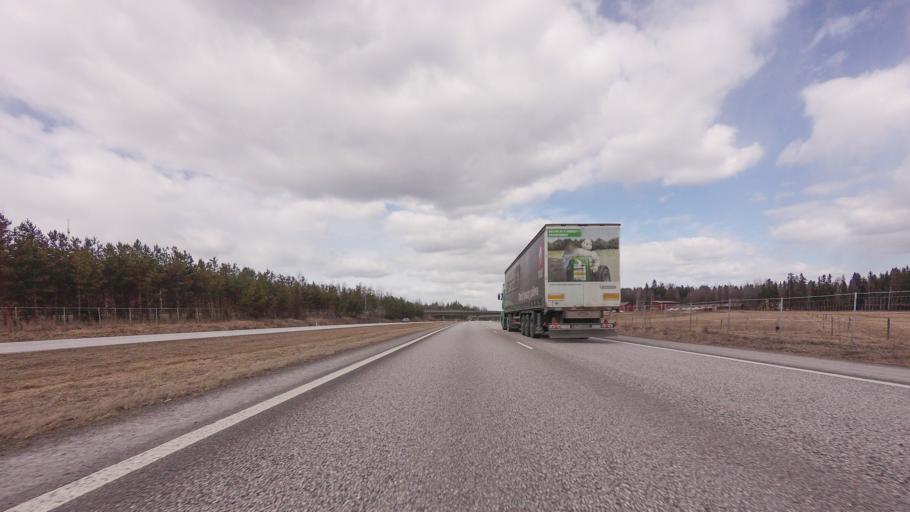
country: FI
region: Uusimaa
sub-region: Helsinki
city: Hyvinge
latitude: 60.5872
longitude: 24.7987
